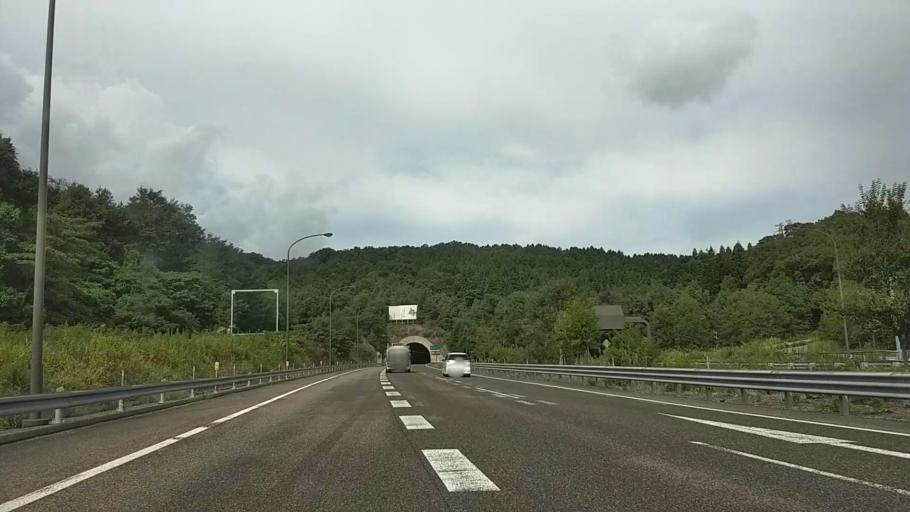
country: JP
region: Niigata
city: Joetsu
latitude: 37.1402
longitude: 138.2126
